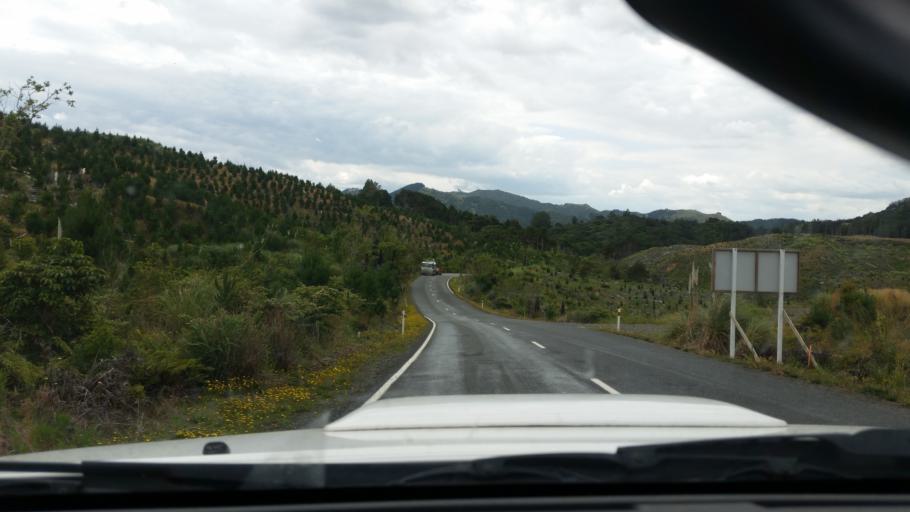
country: NZ
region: Northland
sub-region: Kaipara District
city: Dargaville
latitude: -35.7225
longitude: 173.8588
